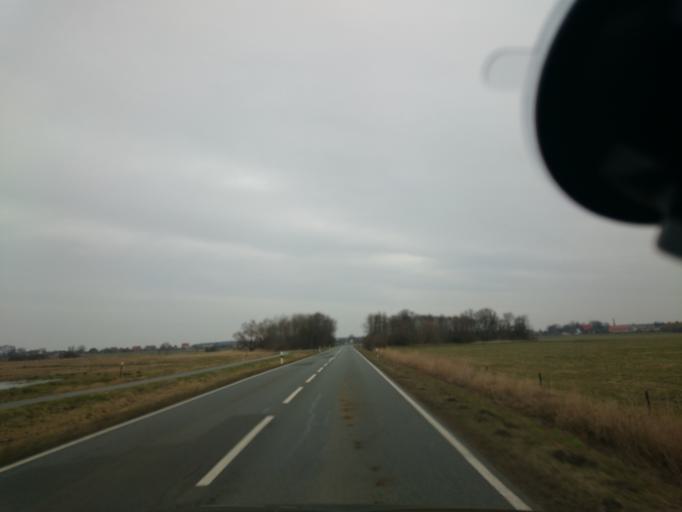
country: DE
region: Mecklenburg-Vorpommern
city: Borgerende-Rethwisch
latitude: 54.1331
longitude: 11.9286
